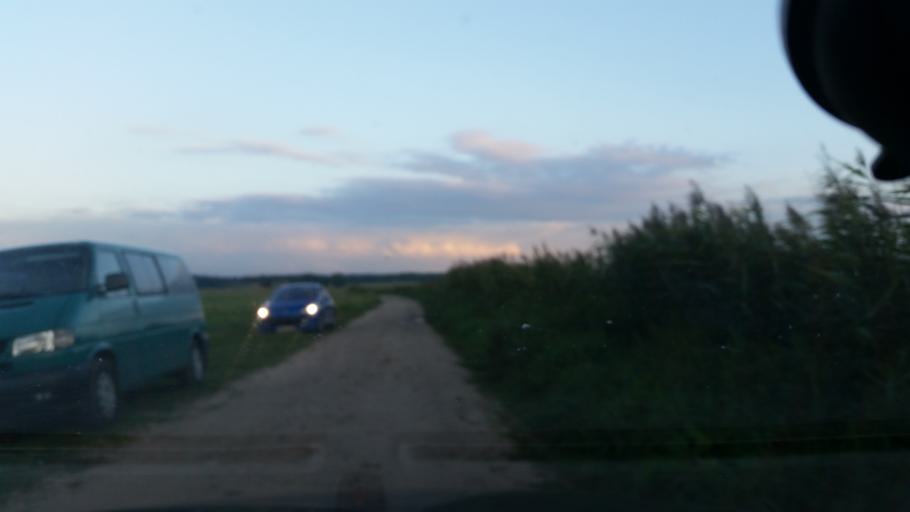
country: PL
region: Pomeranian Voivodeship
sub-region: Powiat wejherowski
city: Choczewo
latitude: 54.7890
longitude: 17.7937
